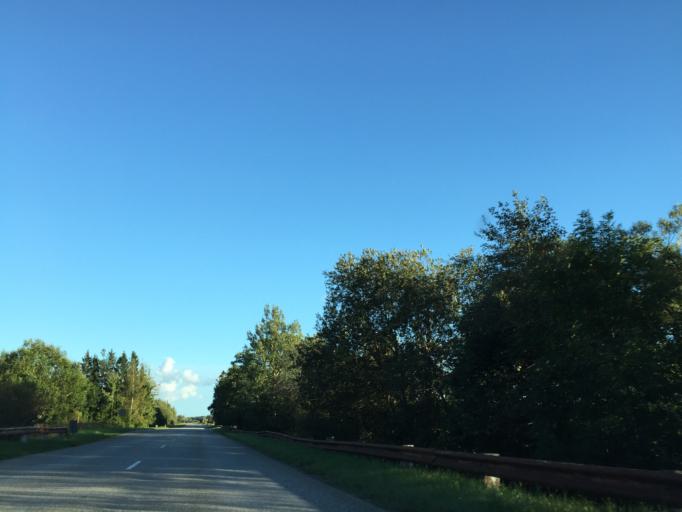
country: LV
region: Kuldigas Rajons
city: Kuldiga
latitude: 56.9428
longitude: 22.0220
